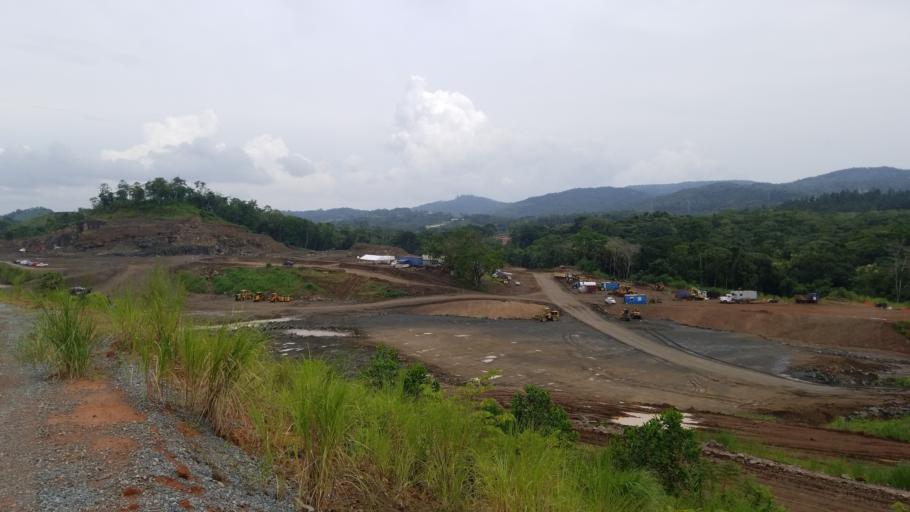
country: PA
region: Panama
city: San Miguelito
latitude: 9.0963
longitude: -79.4664
